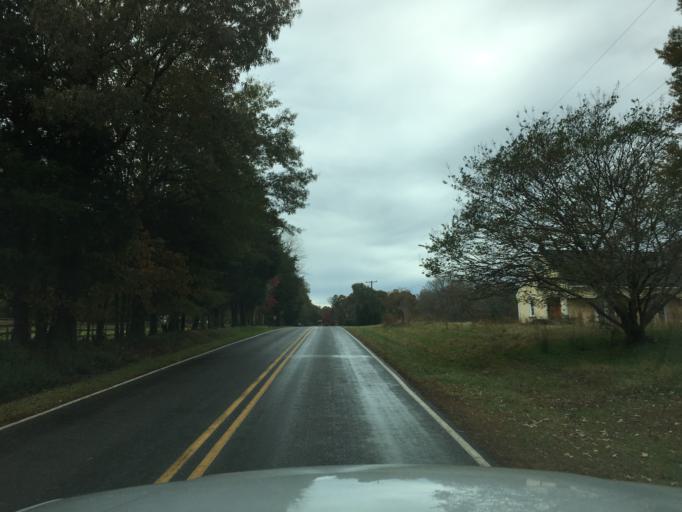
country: US
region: North Carolina
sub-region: Catawba County
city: Maiden
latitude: 35.5992
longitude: -81.2432
